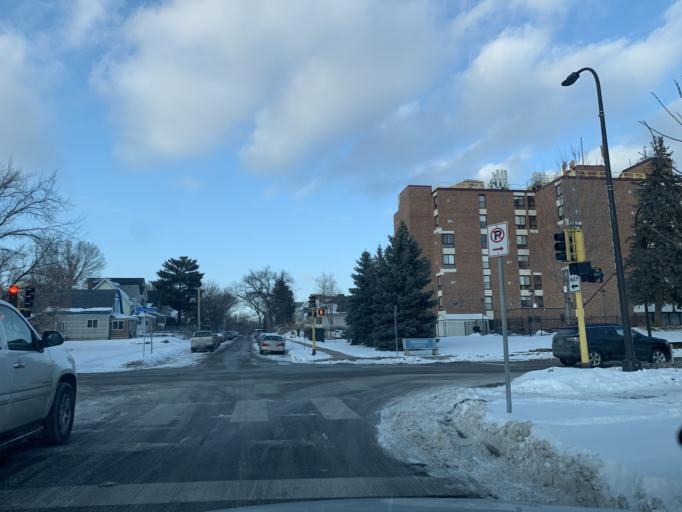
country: US
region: Minnesota
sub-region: Hennepin County
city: Minneapolis
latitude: 44.9913
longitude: -93.3032
